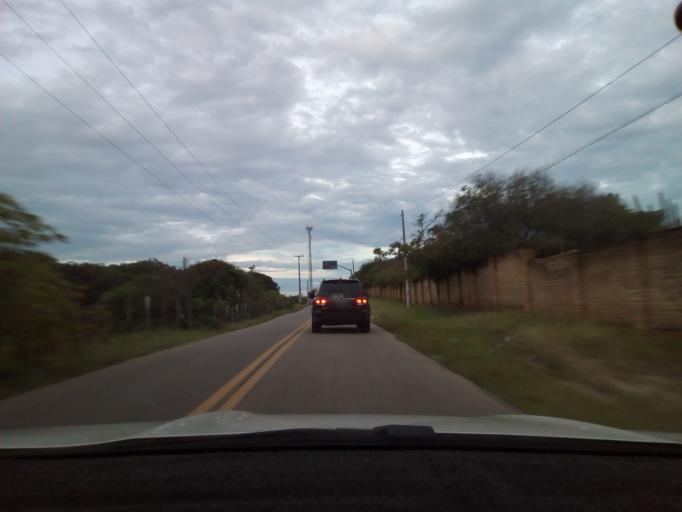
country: BR
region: Ceara
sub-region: Beberibe
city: Beberibe
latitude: -4.1820
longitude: -38.0872
